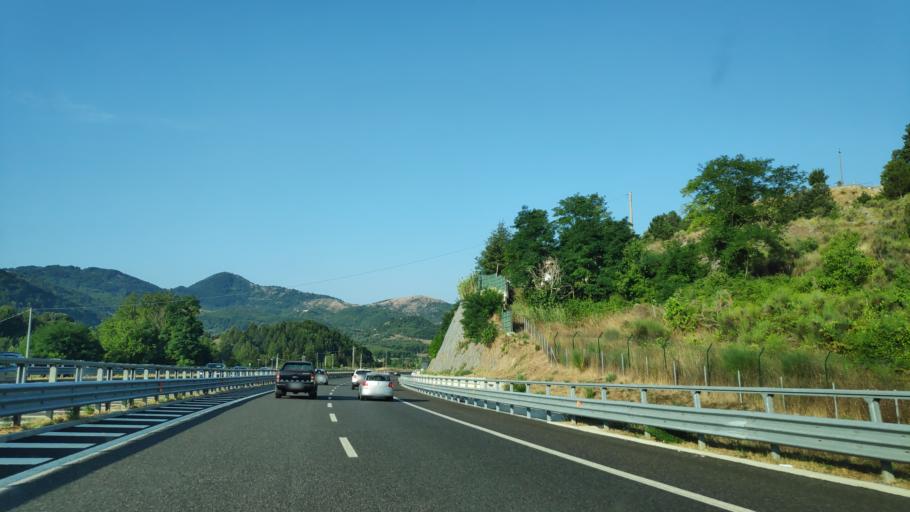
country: IT
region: Calabria
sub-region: Provincia di Cosenza
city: Mormanno
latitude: 39.8802
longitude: 16.0087
